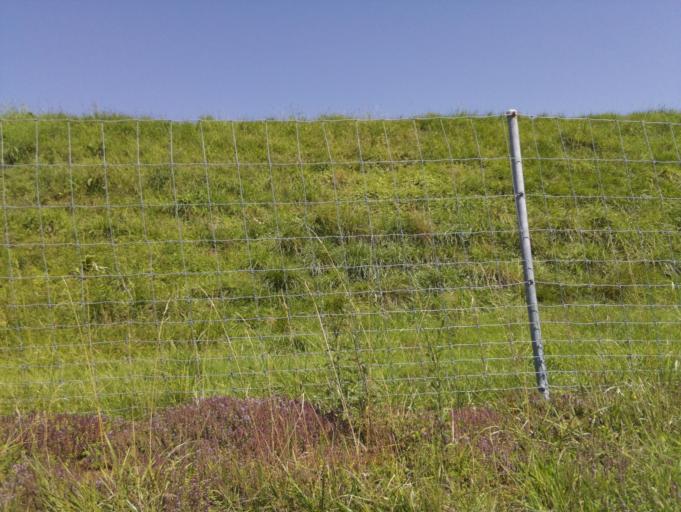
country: CH
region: Schwyz
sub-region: Bezirk March
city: Schubelbach
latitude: 47.1952
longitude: 8.9102
